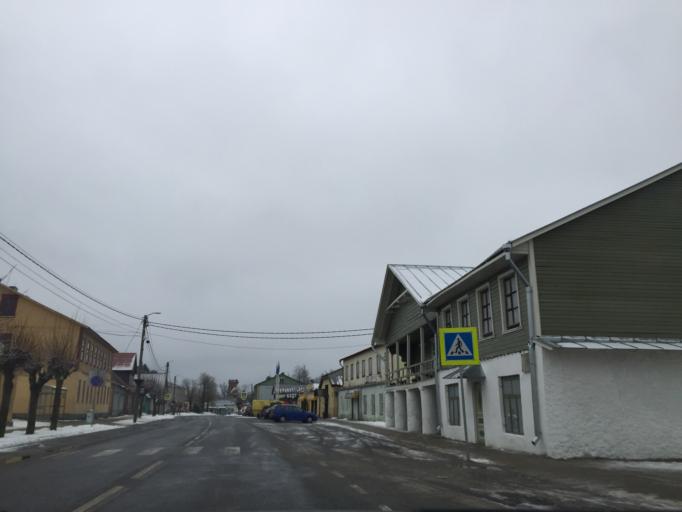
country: EE
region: Laeaene
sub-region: Lihula vald
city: Lihula
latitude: 58.6892
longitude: 23.8354
